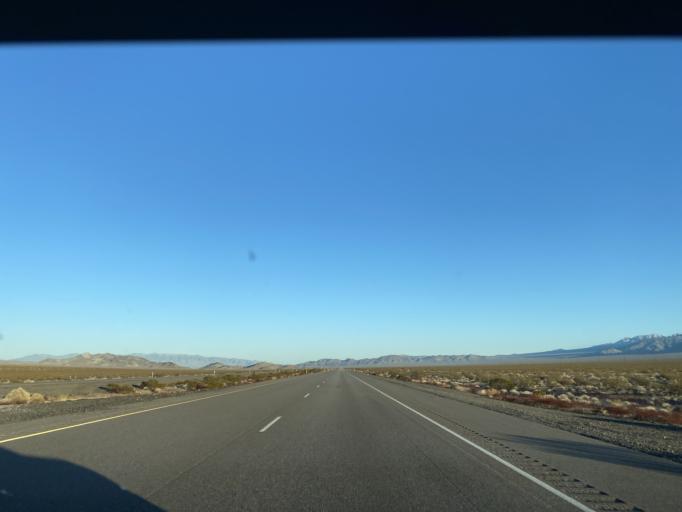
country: US
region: Nevada
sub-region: Nye County
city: Pahrump
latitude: 36.5949
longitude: -115.9453
